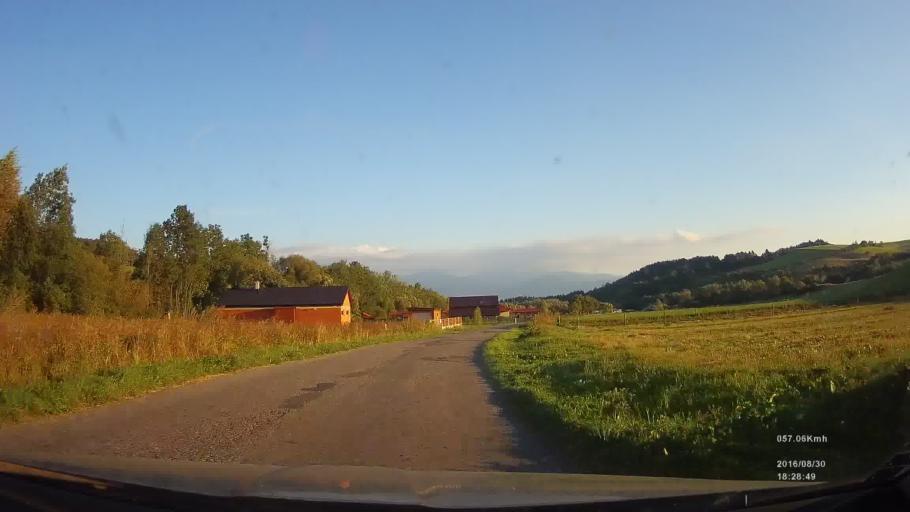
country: SK
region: Zilinsky
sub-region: Okres Liptovsky Mikulas
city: Liptovsky Mikulas
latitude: 49.1379
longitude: 19.5018
